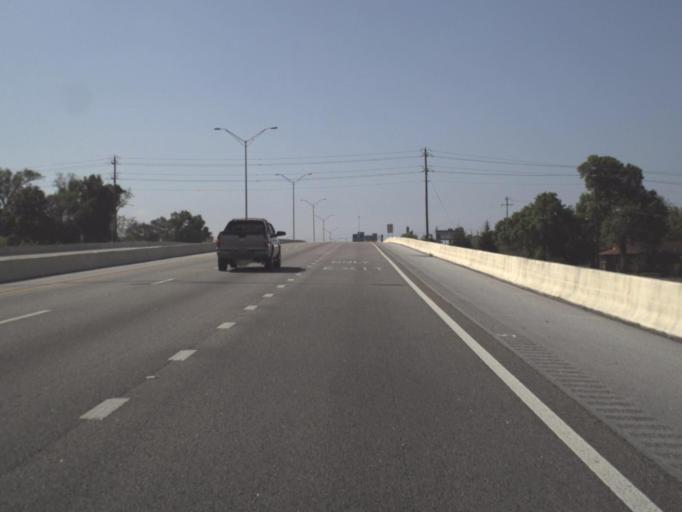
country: US
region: Florida
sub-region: Escambia County
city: Goulding
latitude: 30.4424
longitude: -87.2170
